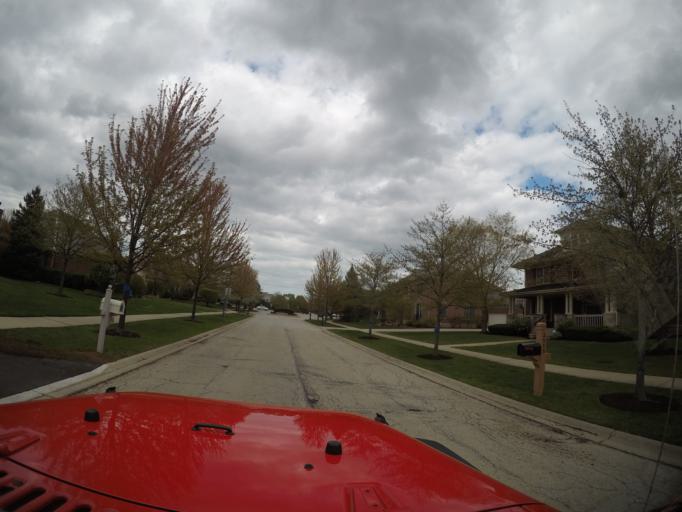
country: US
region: Illinois
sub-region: Cook County
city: Glenview
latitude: 42.0813
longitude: -87.8210
